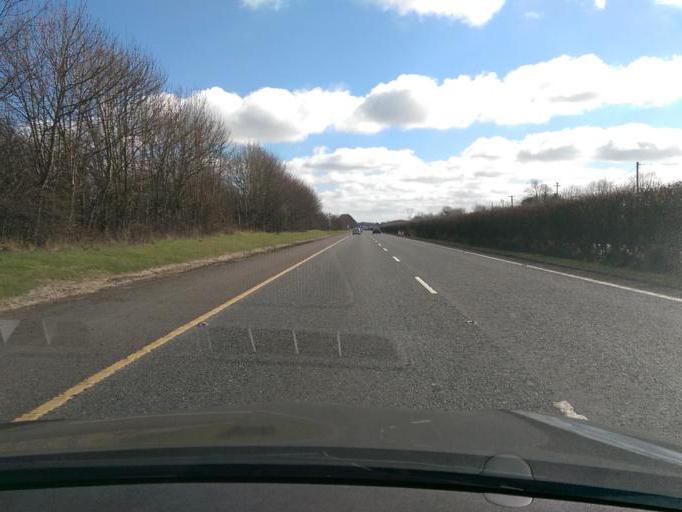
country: IE
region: Leinster
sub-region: Kildare
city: Maynooth
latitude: 53.3753
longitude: -6.6275
